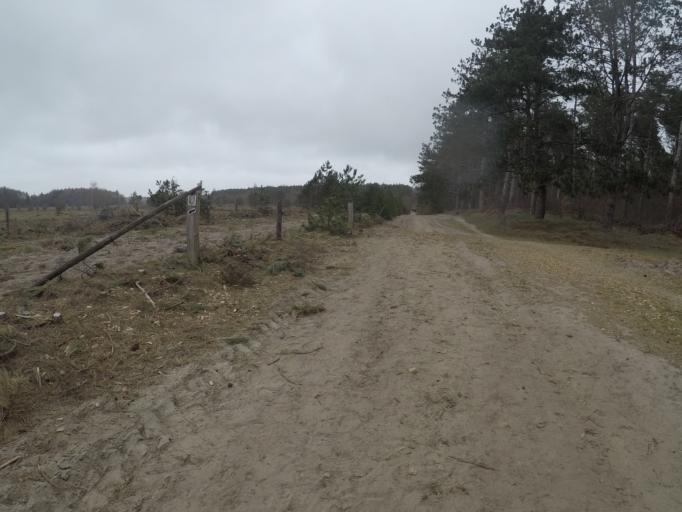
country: DE
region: Lower Saxony
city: Nordholz
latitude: 53.8270
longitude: 8.6446
